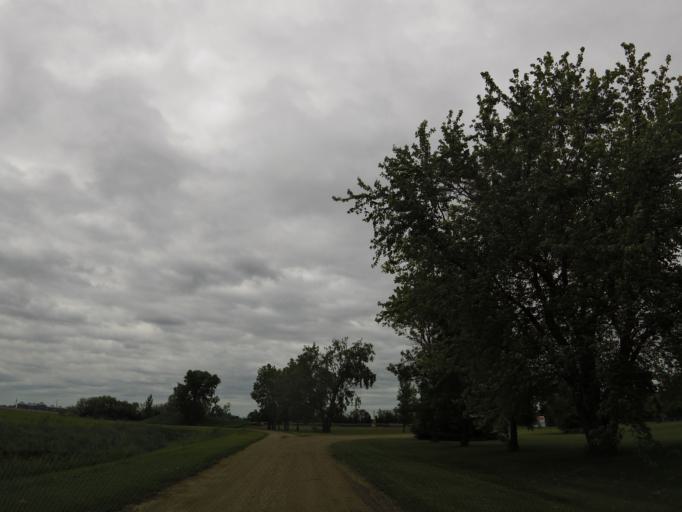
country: US
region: North Dakota
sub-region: Walsh County
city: Grafton
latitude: 48.6185
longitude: -97.4540
